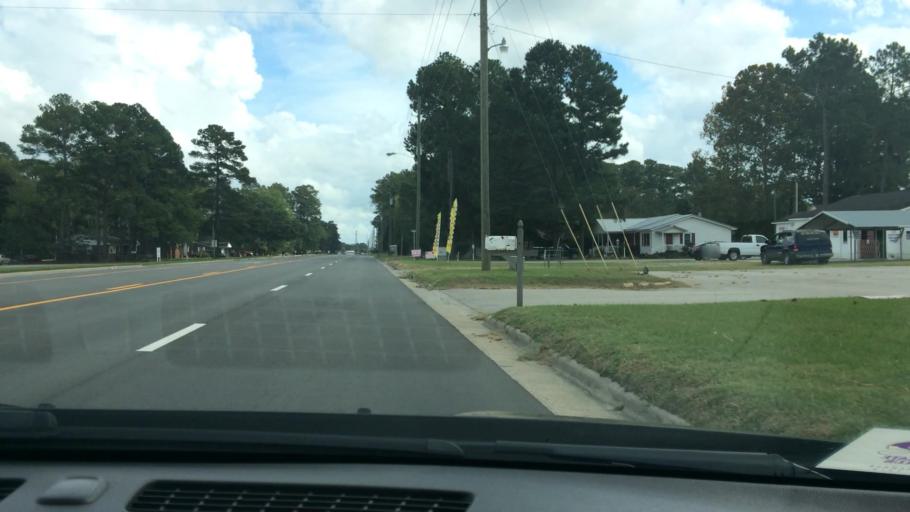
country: US
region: North Carolina
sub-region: Pitt County
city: Farmville
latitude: 35.5908
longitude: -77.6181
